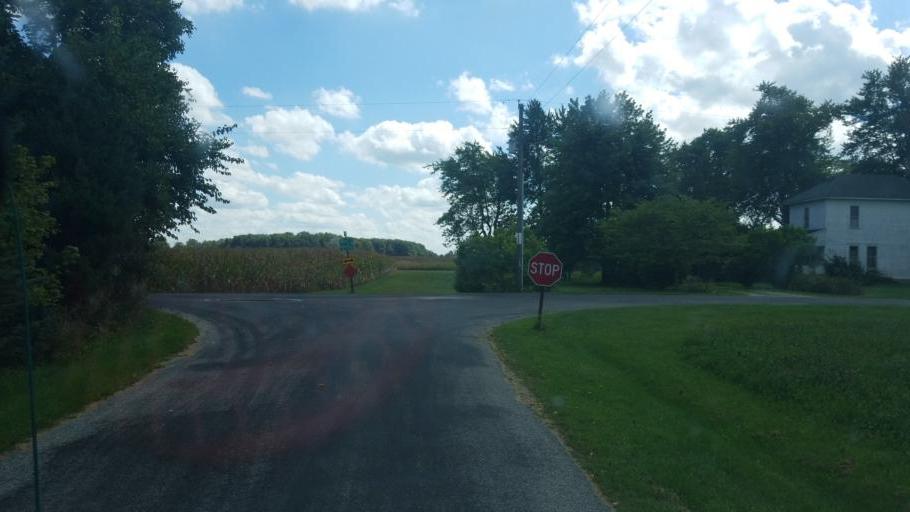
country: US
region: Ohio
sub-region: Union County
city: Richwood
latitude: 40.3651
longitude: -83.2306
